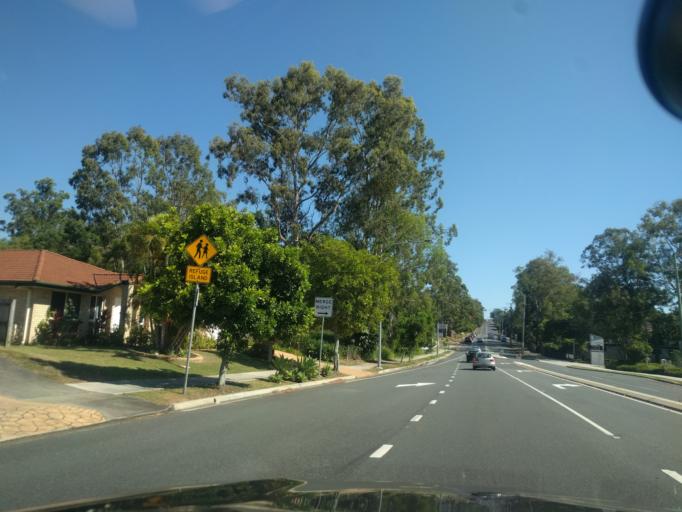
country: AU
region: Queensland
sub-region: Brisbane
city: Chermside West
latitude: -27.3821
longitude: 153.0130
